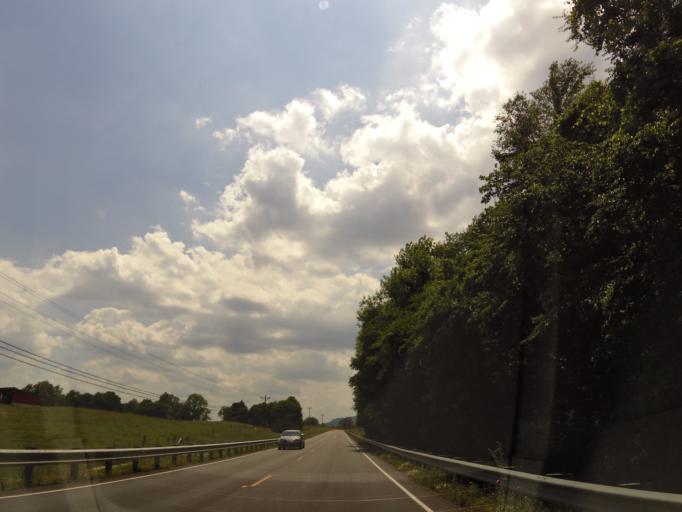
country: US
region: Tennessee
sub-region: Bledsoe County
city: Pikeville
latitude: 35.5699
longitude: -85.2371
